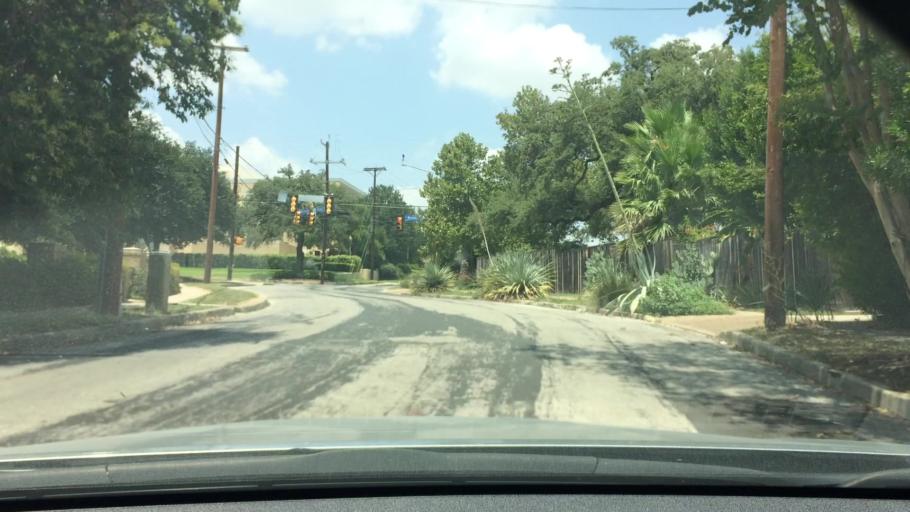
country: US
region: Texas
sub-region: Bexar County
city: Olmos Park
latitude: 29.4562
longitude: -98.4869
